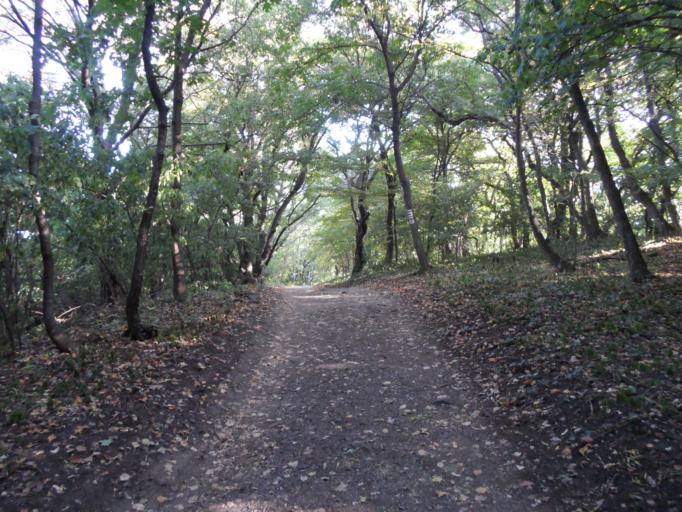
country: HU
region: Veszprem
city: Devecser
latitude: 47.1481
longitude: 17.3689
